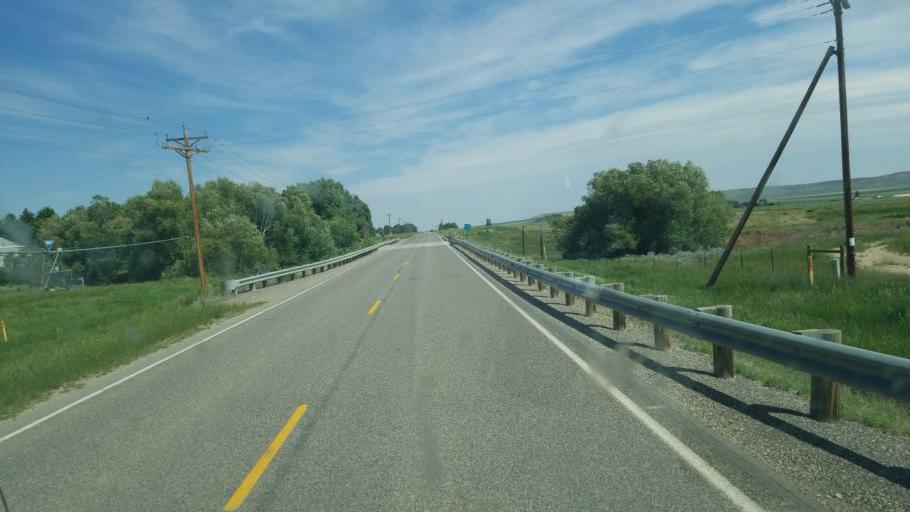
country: US
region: Wyoming
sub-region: Park County
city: Powell
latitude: 44.7429
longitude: -108.9327
